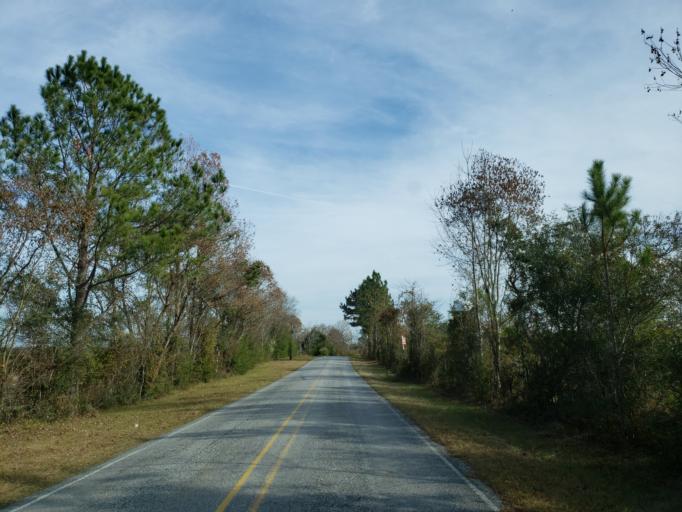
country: US
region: Mississippi
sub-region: Forrest County
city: Rawls Springs
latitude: 31.4077
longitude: -89.4023
